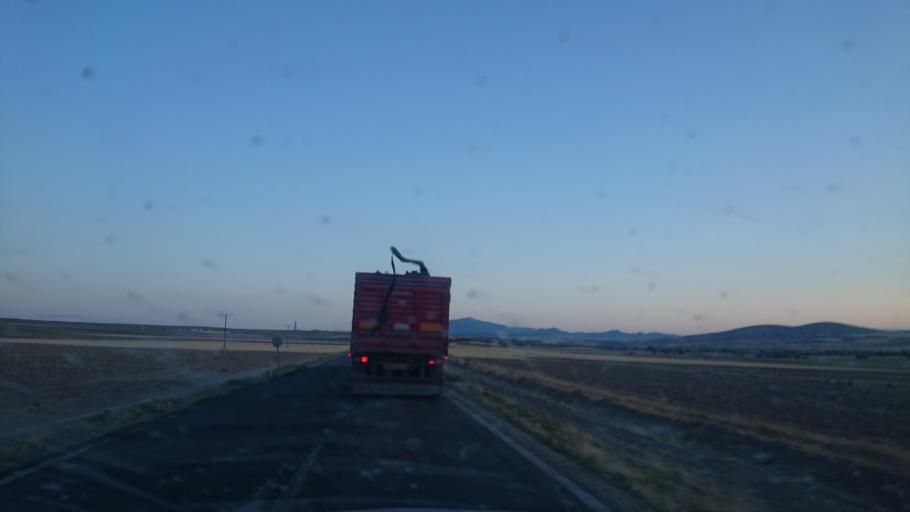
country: TR
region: Aksaray
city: Balci
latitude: 38.8170
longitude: 34.1344
